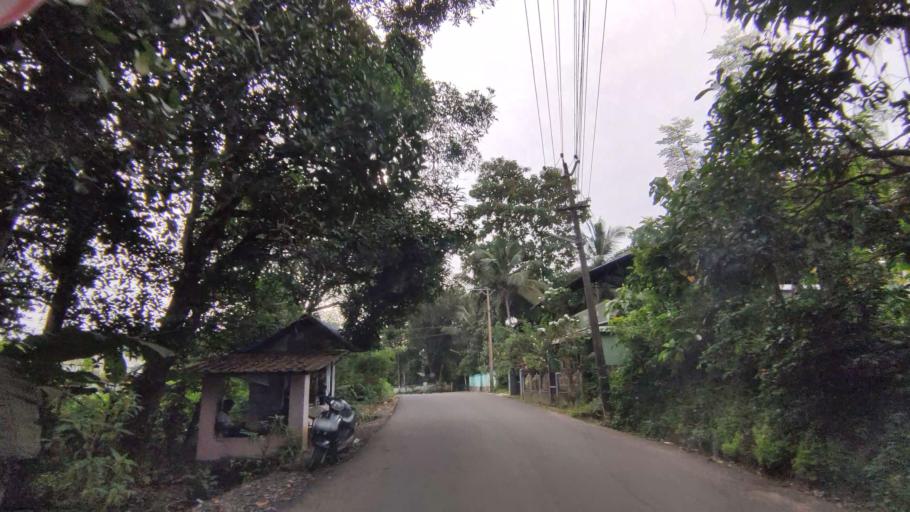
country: IN
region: Kerala
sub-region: Kottayam
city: Kottayam
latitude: 9.6644
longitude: 76.5182
